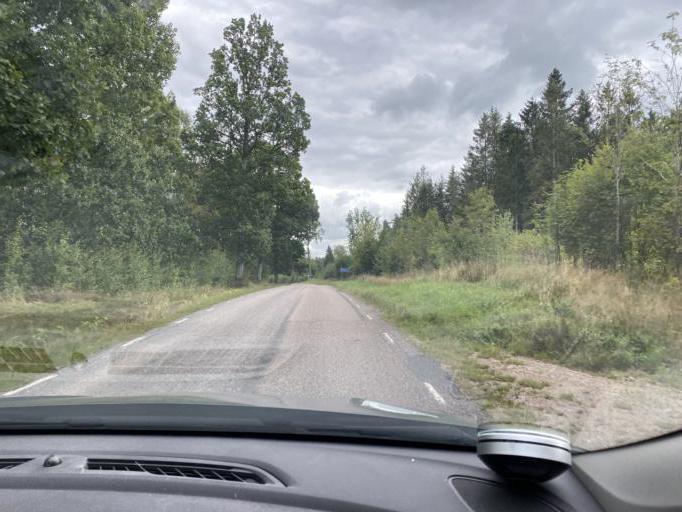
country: SE
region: Kronoberg
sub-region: Markaryds Kommun
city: Markaryd
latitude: 56.4862
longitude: 13.5575
